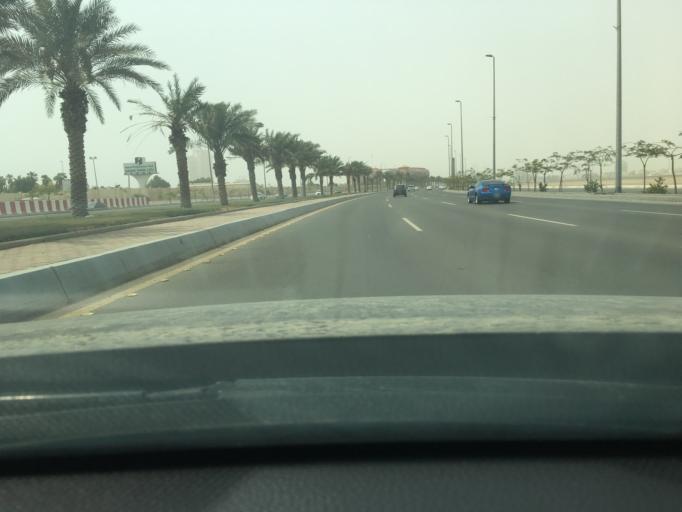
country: SA
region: Makkah
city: Jeddah
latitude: 21.6308
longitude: 39.1127
